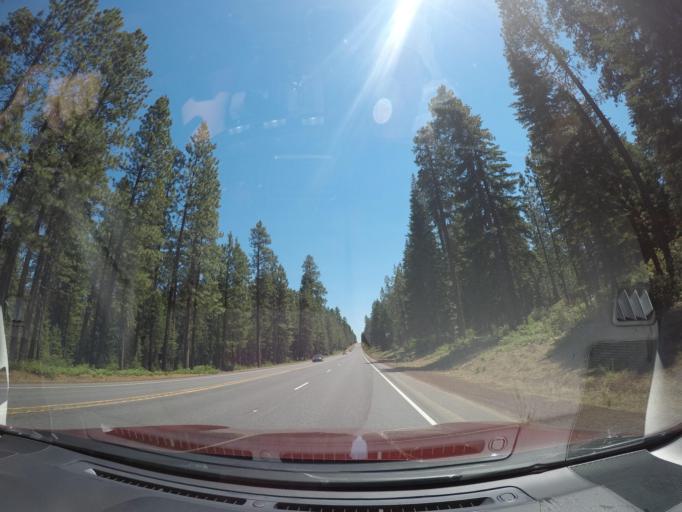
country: US
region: Oregon
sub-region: Deschutes County
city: Sisters
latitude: 44.4140
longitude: -121.6973
